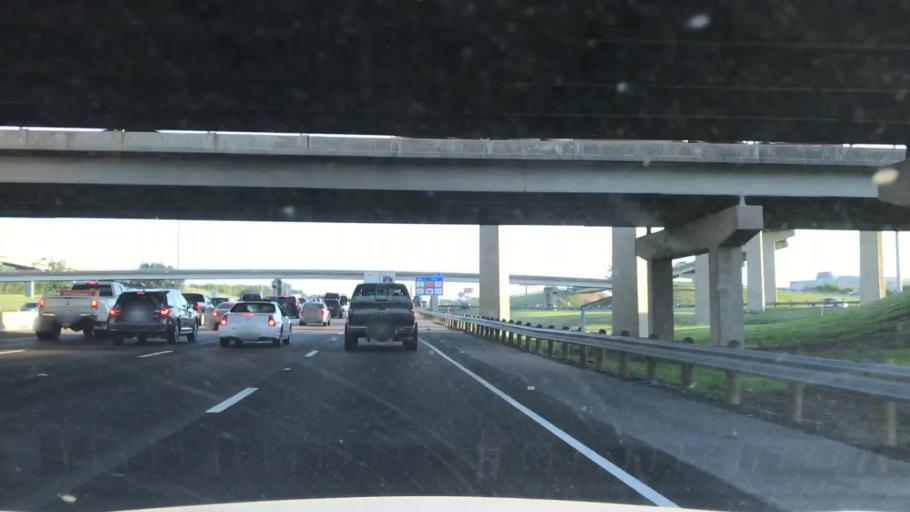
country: US
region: Texas
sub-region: Dallas County
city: Mesquite
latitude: 32.7927
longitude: -96.6253
